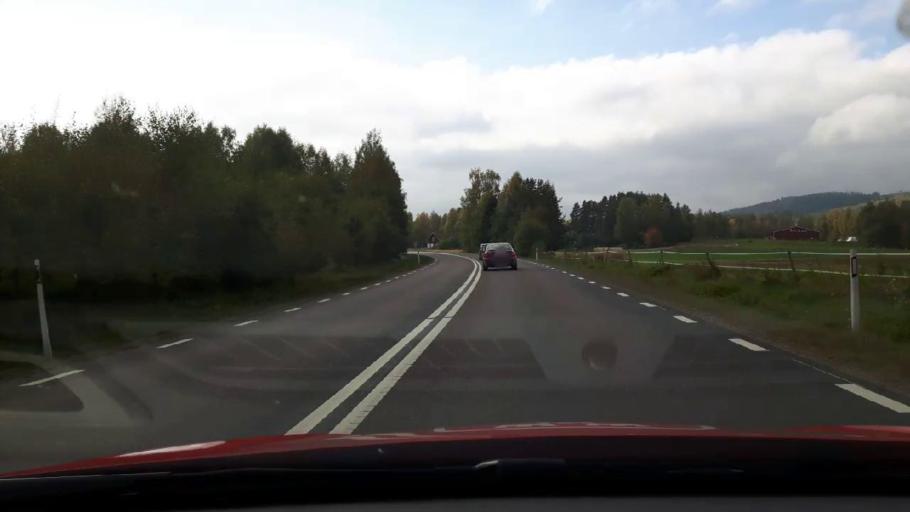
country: SE
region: Gaevleborg
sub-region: Bollnas Kommun
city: Arbra
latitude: 61.4860
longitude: 16.3687
